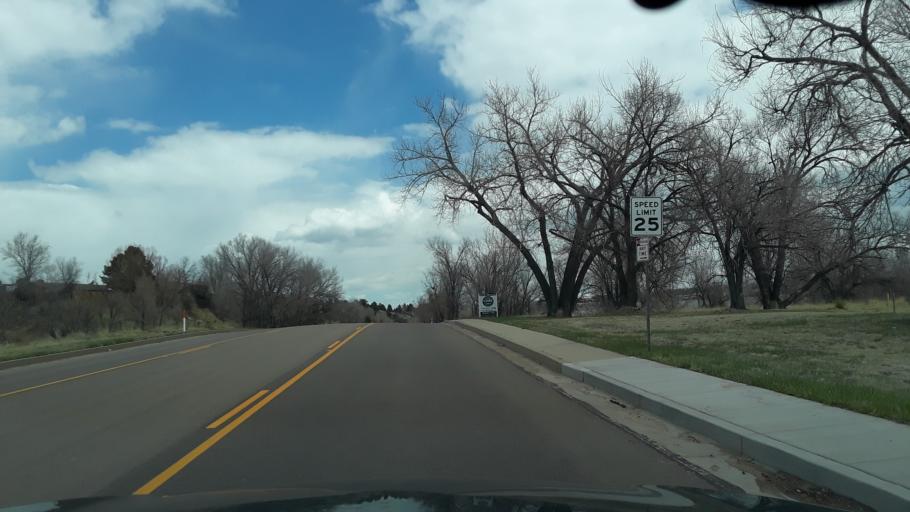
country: US
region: Colorado
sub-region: El Paso County
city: Colorado Springs
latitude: 38.9183
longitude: -104.8208
